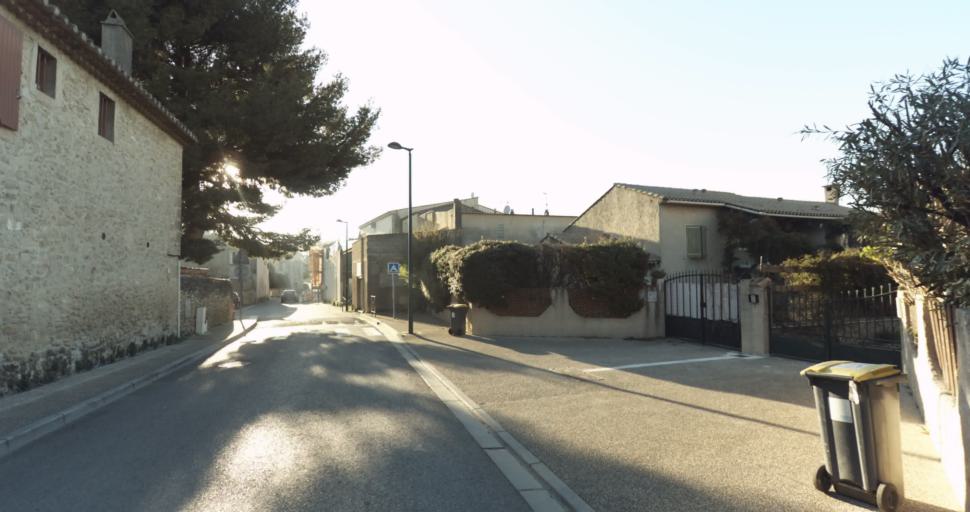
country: FR
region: Provence-Alpes-Cote d'Azur
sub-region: Departement des Bouches-du-Rhone
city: Pelissanne
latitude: 43.6292
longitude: 5.1493
